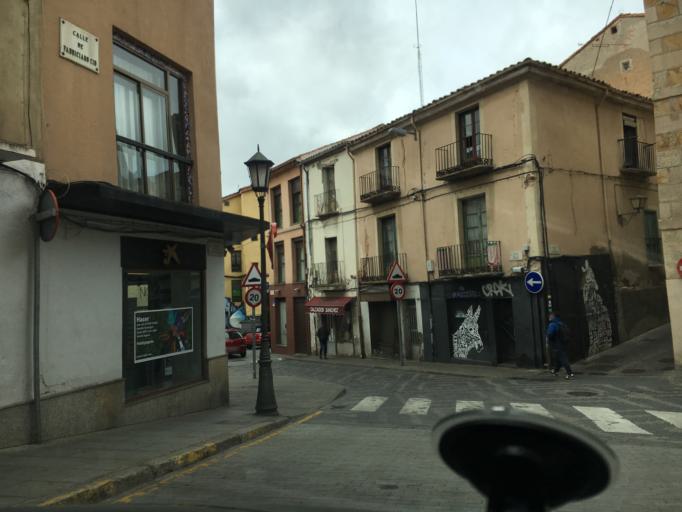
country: ES
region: Castille and Leon
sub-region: Provincia de Zamora
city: Zamora
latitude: 41.5048
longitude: -5.7477
